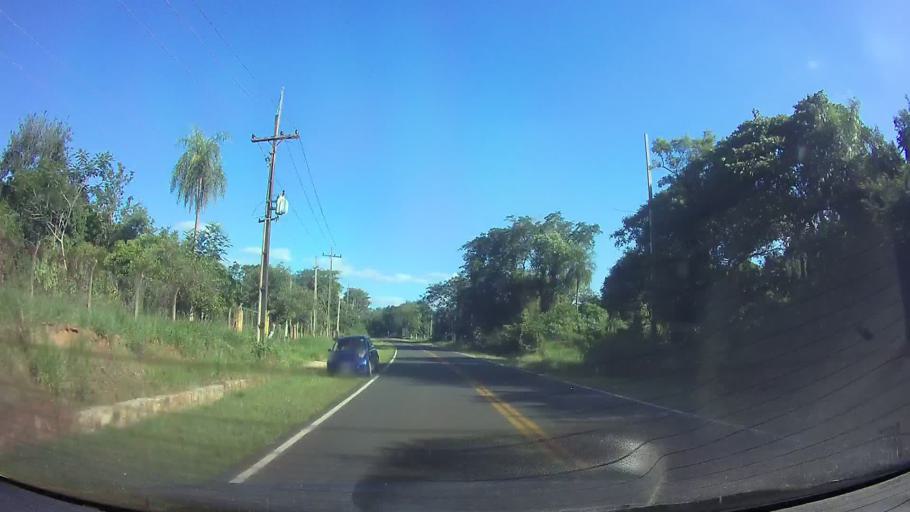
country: PY
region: Cordillera
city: Atyra
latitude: -25.3047
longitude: -57.1578
